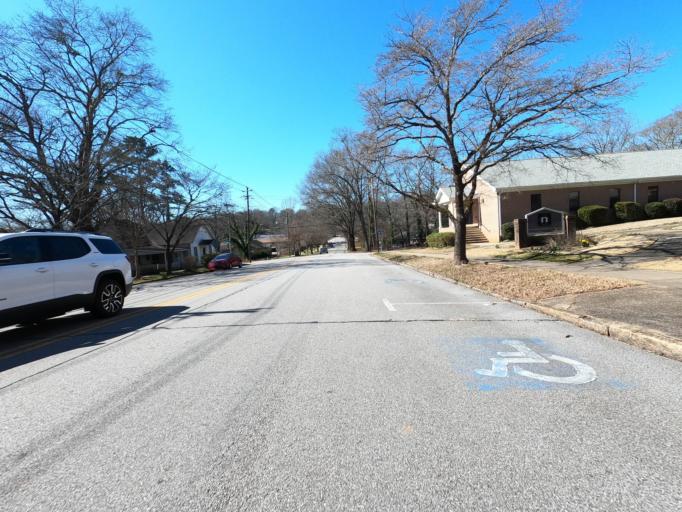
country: US
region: Georgia
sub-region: Clarke County
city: Athens
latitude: 33.9664
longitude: -83.3963
